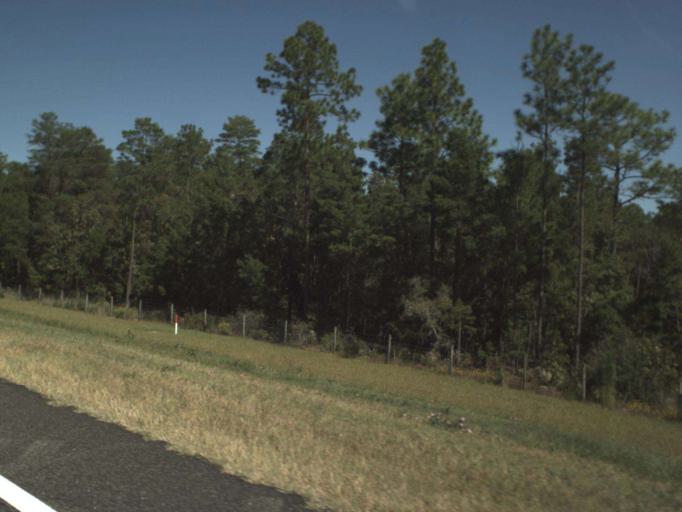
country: US
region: Florida
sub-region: Okaloosa County
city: Niceville
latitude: 30.5299
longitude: -86.4185
